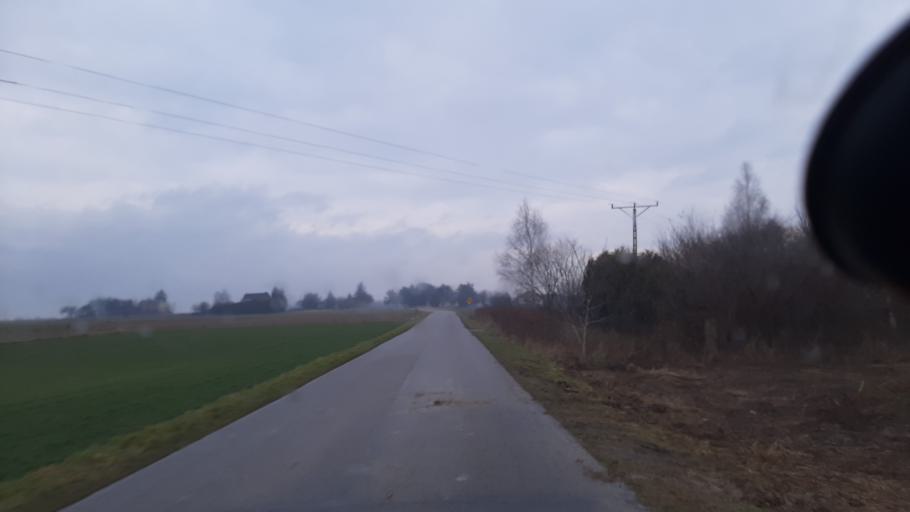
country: PL
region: Lublin Voivodeship
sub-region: Powiat lubelski
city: Niemce
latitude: 51.3320
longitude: 22.5872
